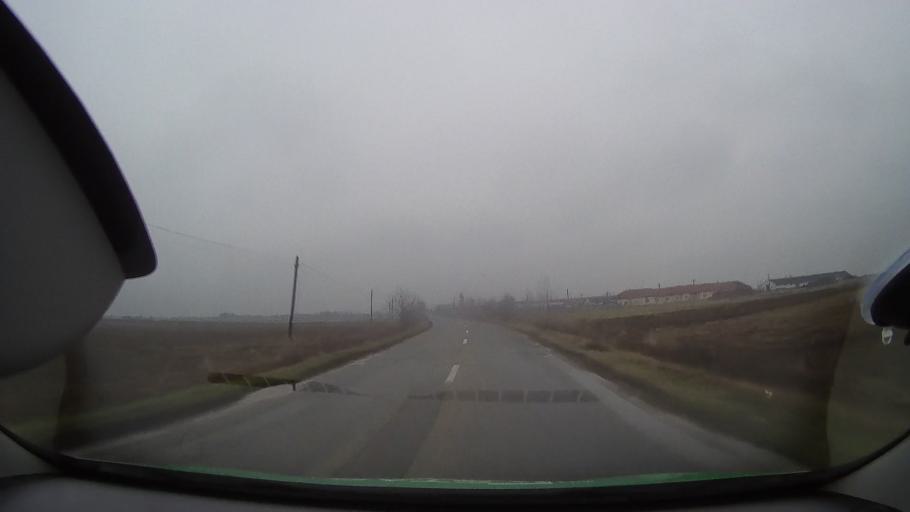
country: RO
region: Bihor
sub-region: Comuna Tulca
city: Tulca
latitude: 46.7929
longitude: 21.7521
